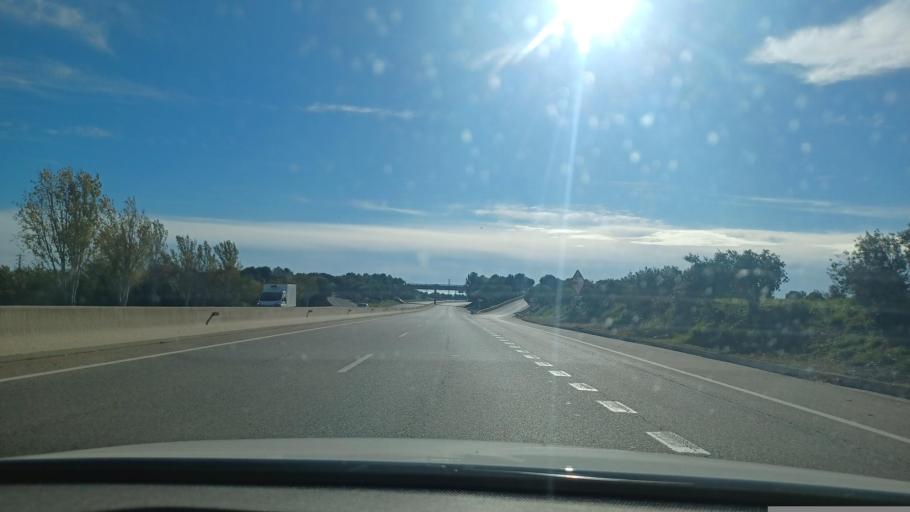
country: ES
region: Catalonia
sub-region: Provincia de Tarragona
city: Reus
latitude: 41.1579
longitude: 1.1424
